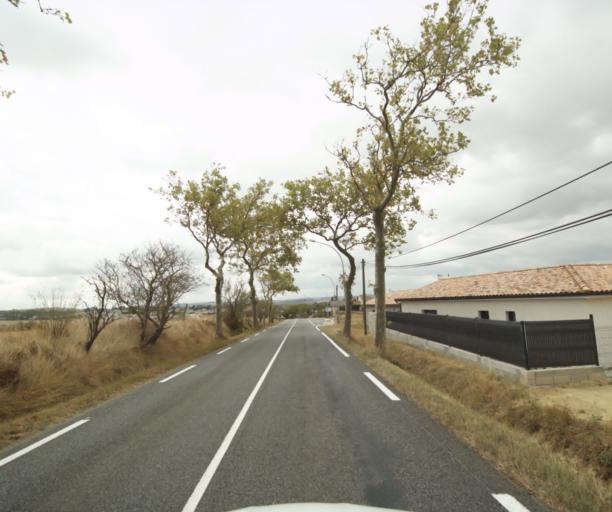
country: FR
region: Midi-Pyrenees
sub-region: Departement de la Haute-Garonne
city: Villefranche-de-Lauragais
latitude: 43.4122
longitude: 1.7160
